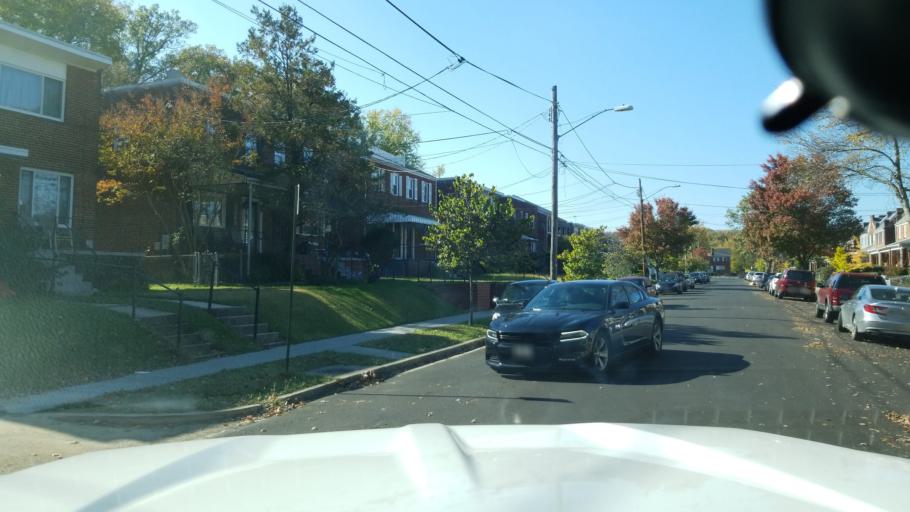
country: US
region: Maryland
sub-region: Prince George's County
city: Chillum
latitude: 38.9494
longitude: -76.9869
